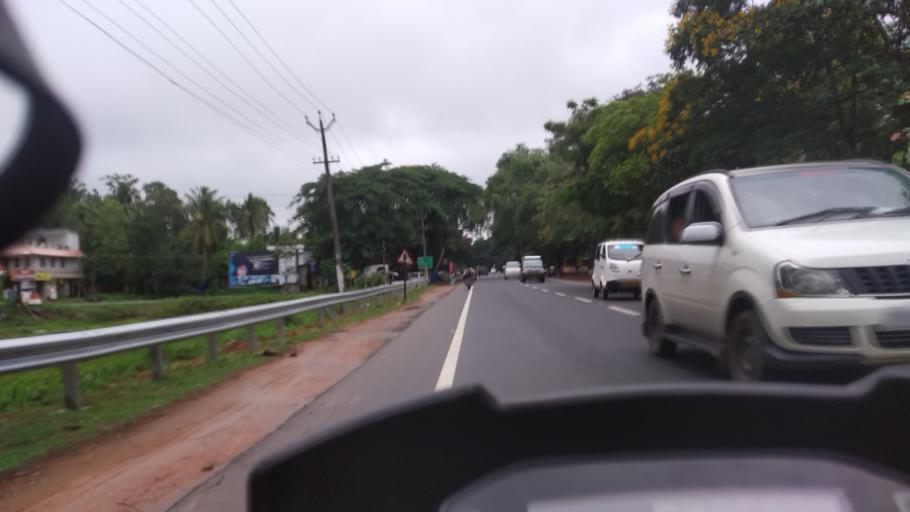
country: IN
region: Kerala
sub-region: Alappuzha
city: Mavelikara
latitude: 9.3058
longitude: 76.4321
